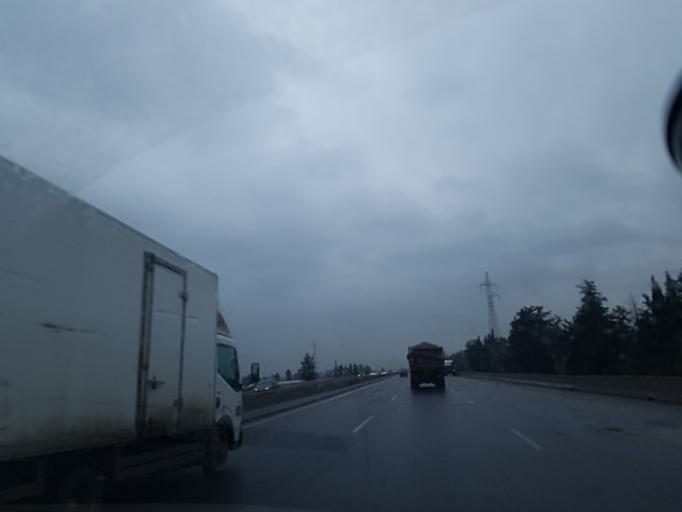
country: DZ
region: Blida
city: Meftah
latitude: 36.6607
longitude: 3.2641
